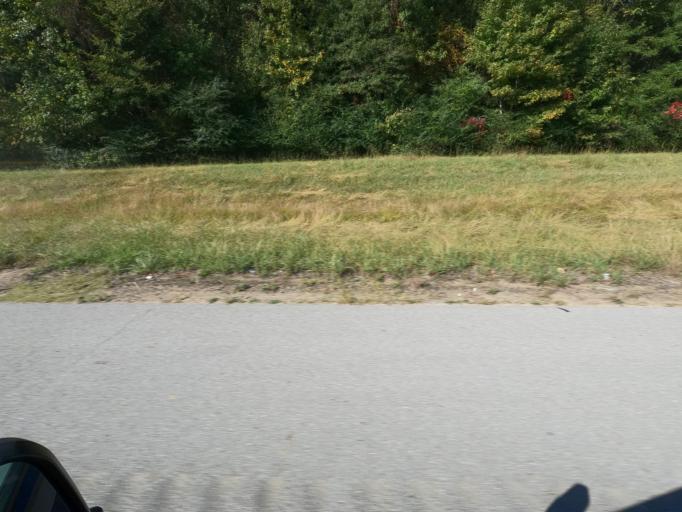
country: US
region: Tennessee
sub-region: Shelby County
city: Arlington
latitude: 35.2674
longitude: -89.6790
